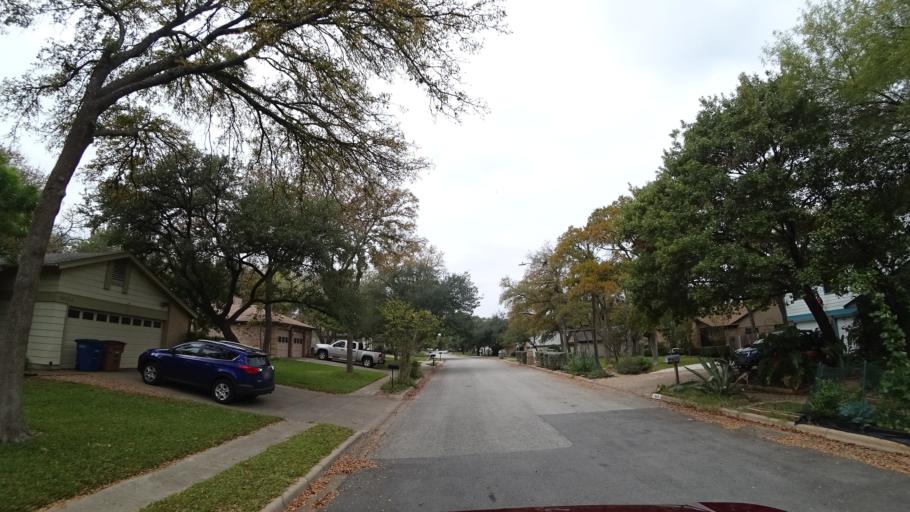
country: US
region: Texas
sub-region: Travis County
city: Wells Branch
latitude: 30.4313
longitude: -97.7140
